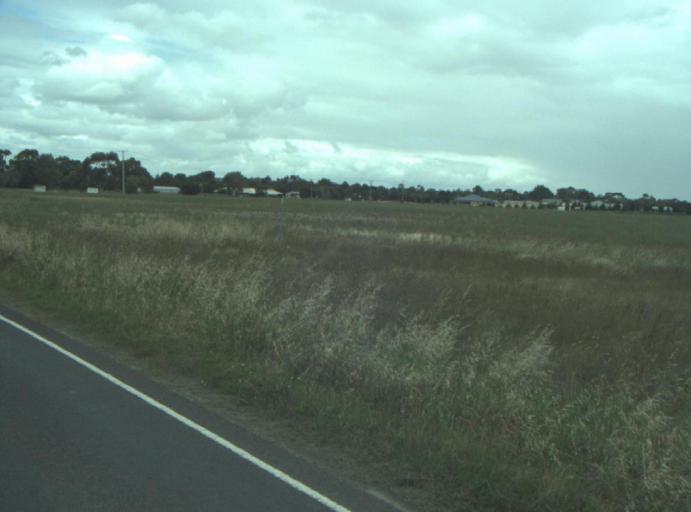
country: AU
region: Victoria
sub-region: Greater Geelong
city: Lara
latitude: -38.0137
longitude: 144.4533
